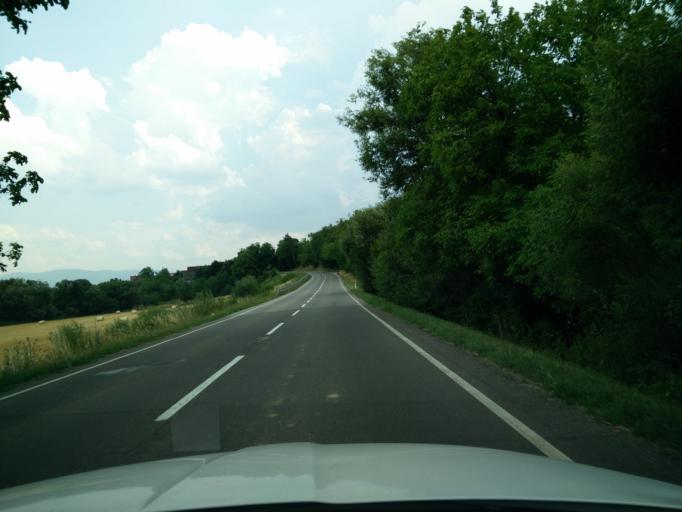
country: SK
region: Nitriansky
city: Novaky
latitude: 48.7716
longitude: 18.4904
